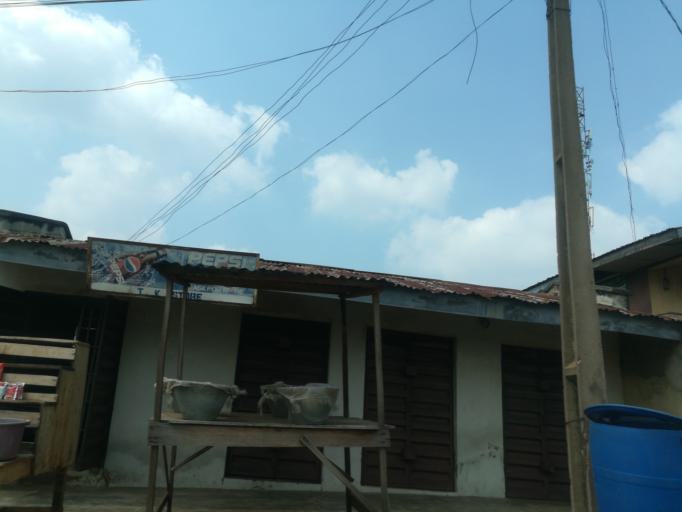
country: NG
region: Oyo
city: Ibadan
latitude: 7.3954
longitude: 3.9059
